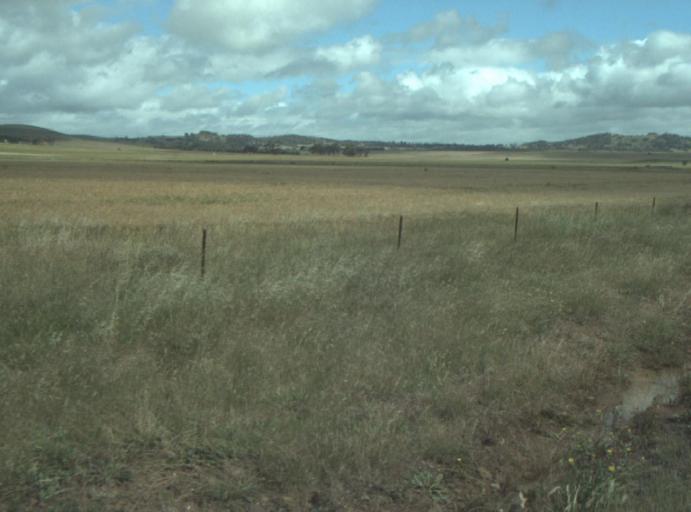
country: AU
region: Victoria
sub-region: Greater Geelong
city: Lara
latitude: -37.9129
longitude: 144.3151
